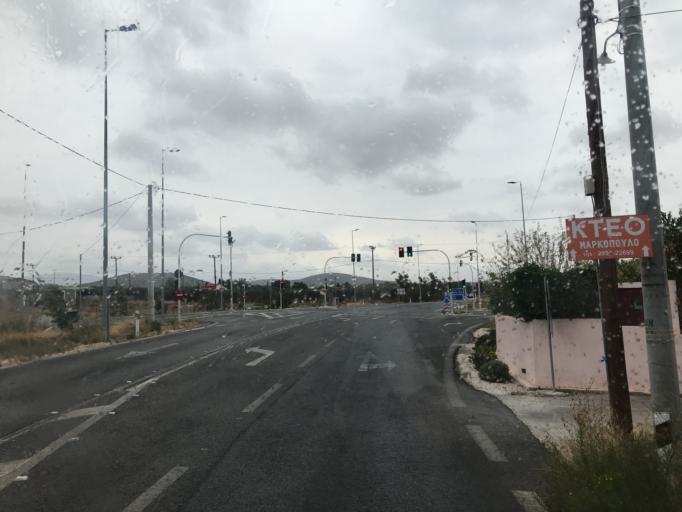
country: GR
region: Attica
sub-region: Nomarchia Anatolikis Attikis
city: Kalyvia Thorikou
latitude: 37.8282
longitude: 23.9057
